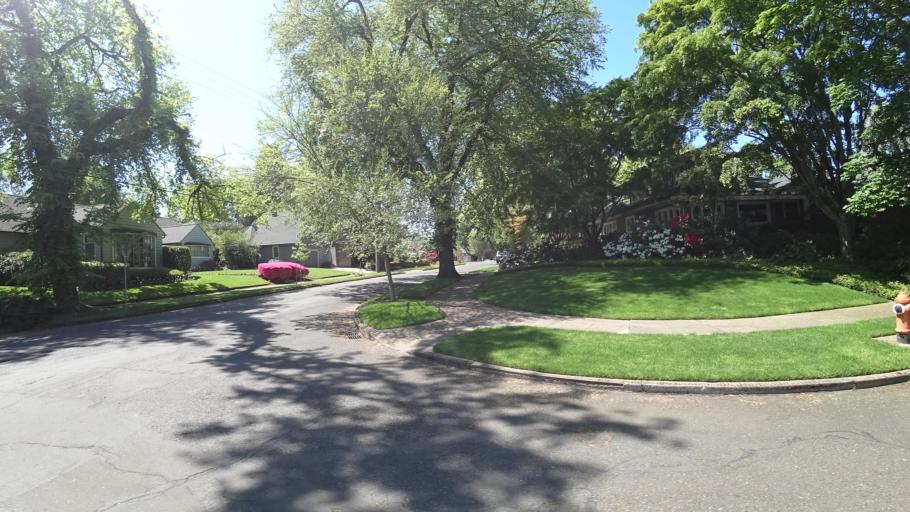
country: US
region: Oregon
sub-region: Clackamas County
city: Milwaukie
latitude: 45.4679
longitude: -122.6304
